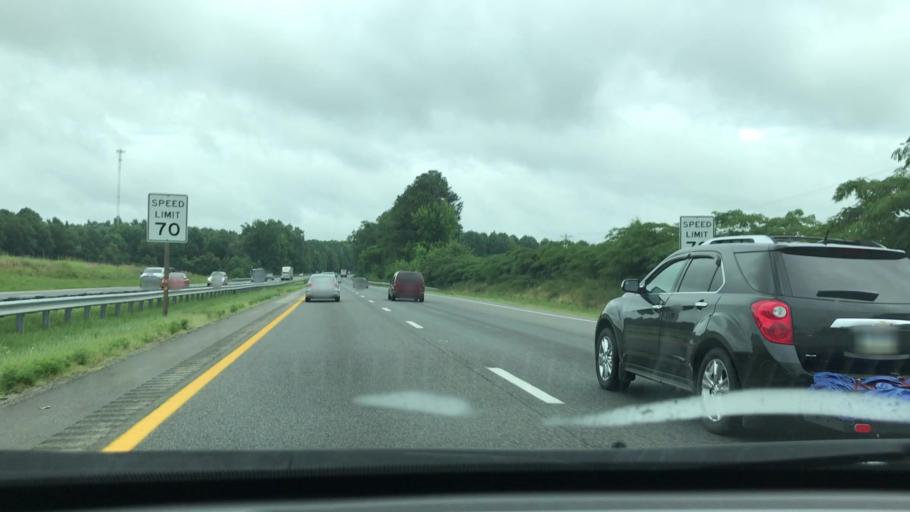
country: US
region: Virginia
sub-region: City of Emporia
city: Emporia
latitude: 36.7059
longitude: -77.5476
